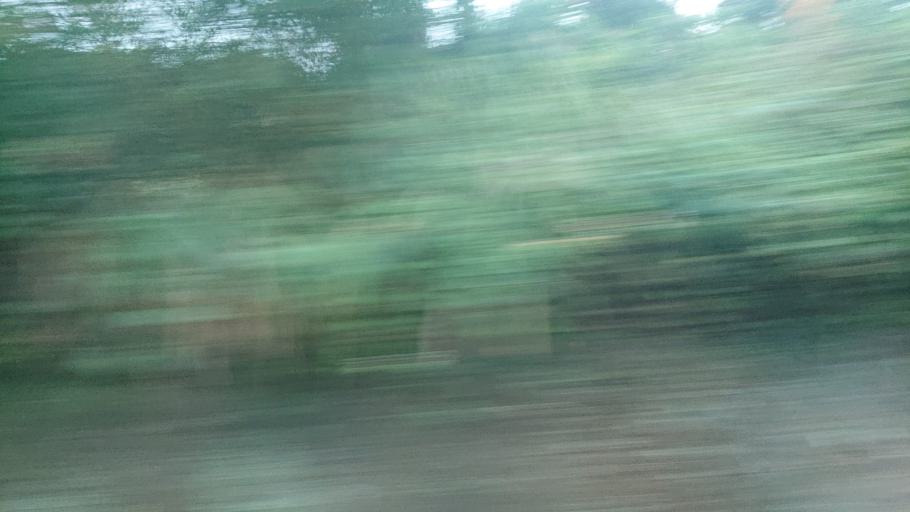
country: TW
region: Taiwan
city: Lugu
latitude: 23.5240
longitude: 120.7076
